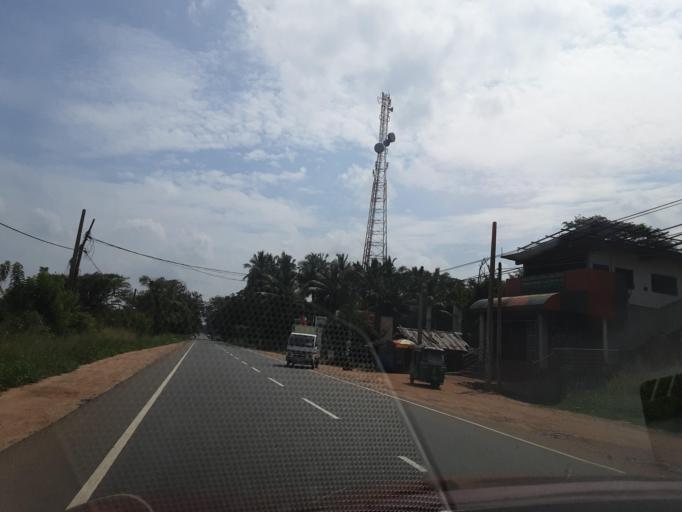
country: LK
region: Northern Province
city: Vavuniya
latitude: 8.5290
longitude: 80.4986
